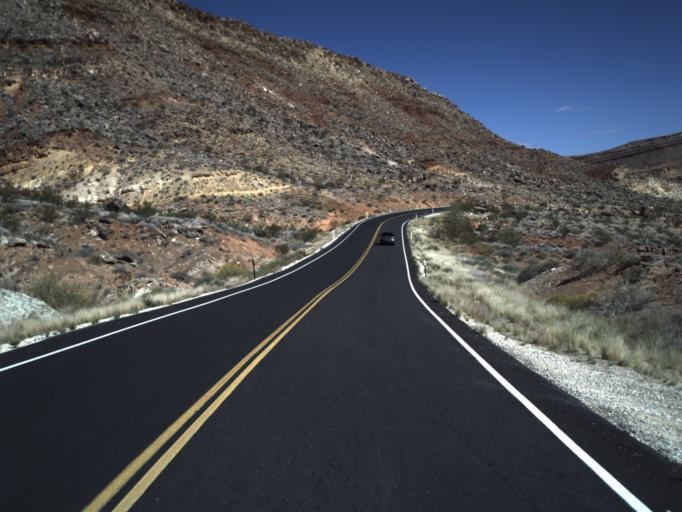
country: US
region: Utah
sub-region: Washington County
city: Hurricane
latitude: 37.1846
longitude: -113.3977
